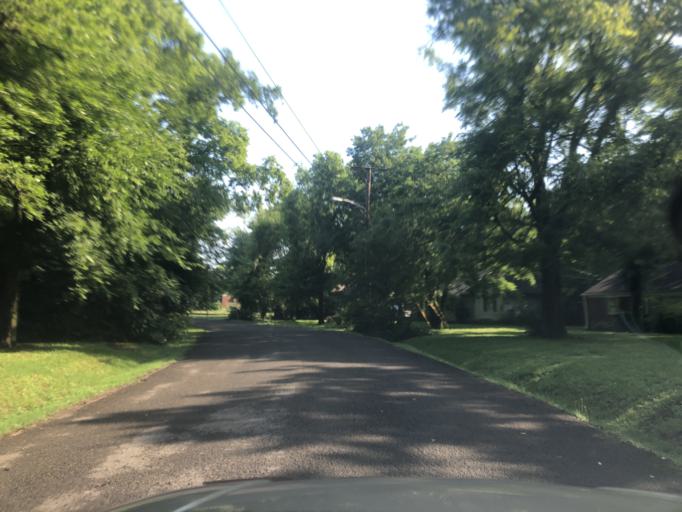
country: US
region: Tennessee
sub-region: Davidson County
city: Lakewood
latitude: 36.2291
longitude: -86.7153
